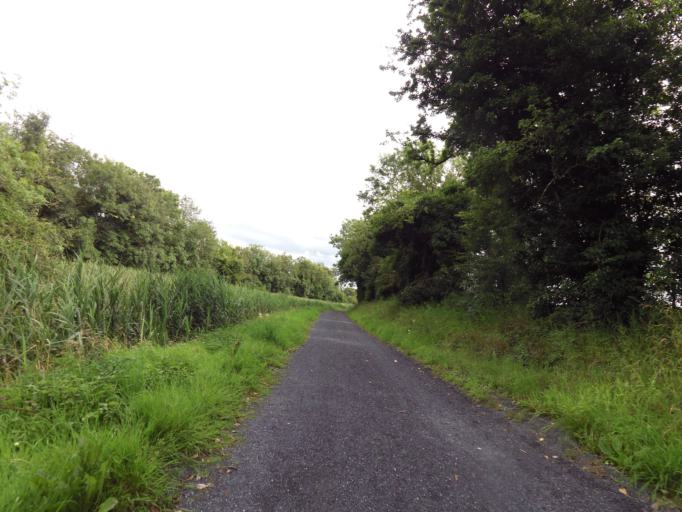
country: IE
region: Leinster
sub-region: An Iarmhi
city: An Muileann gCearr
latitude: 53.5551
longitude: -7.4796
